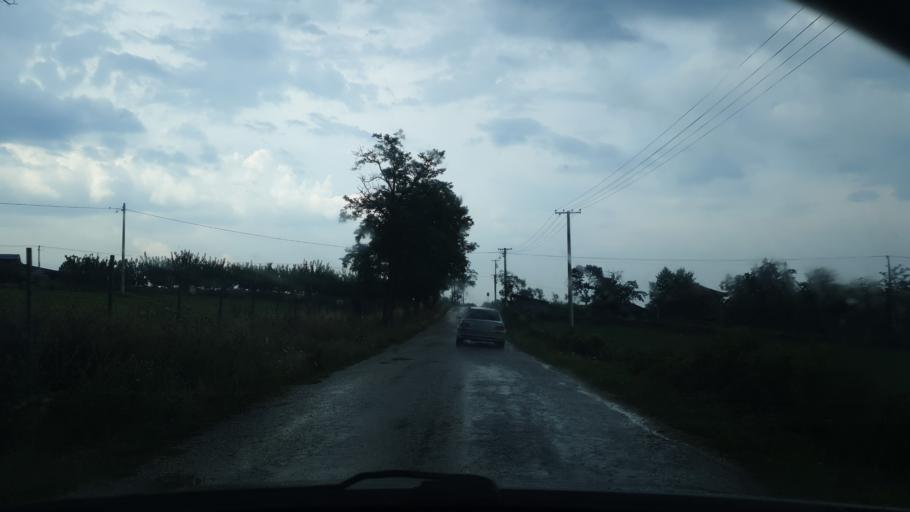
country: RS
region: Central Serbia
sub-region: Sumadijski Okrug
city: Kragujevac
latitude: 44.0741
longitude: 20.7893
